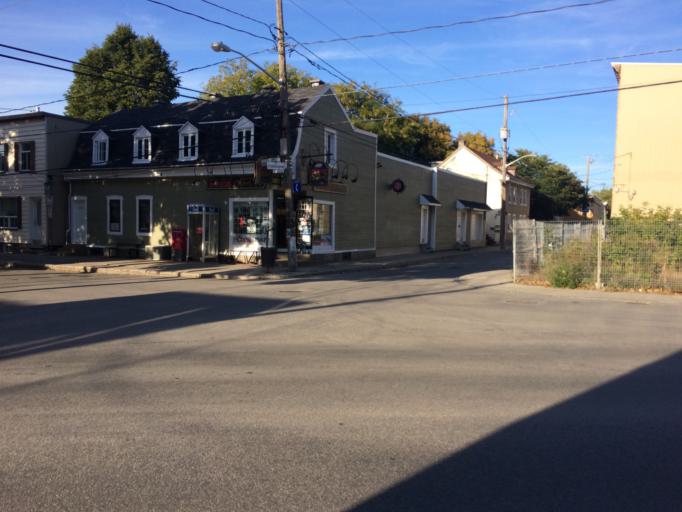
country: CA
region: Quebec
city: Quebec
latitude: 46.8068
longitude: -71.2354
